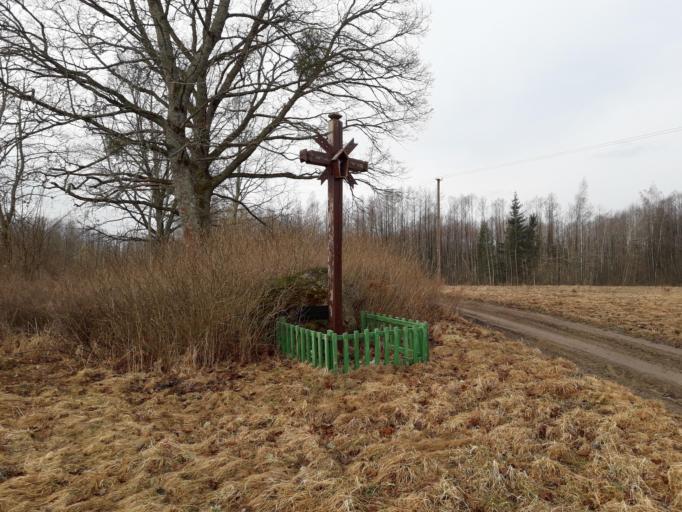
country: LT
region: Alytaus apskritis
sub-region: Alytus
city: Alytus
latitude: 54.2483
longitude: 24.1472
